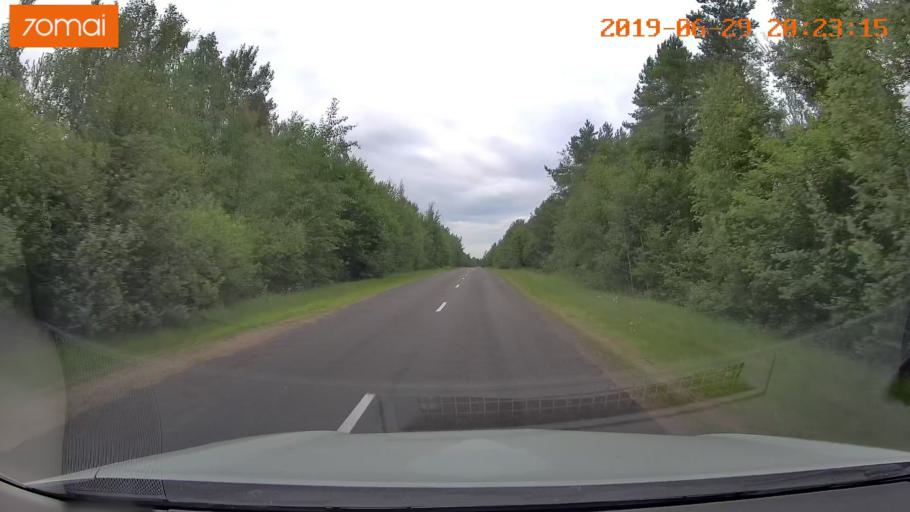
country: BY
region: Brest
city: Asnyezhytsy
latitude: 52.4421
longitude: 26.2595
